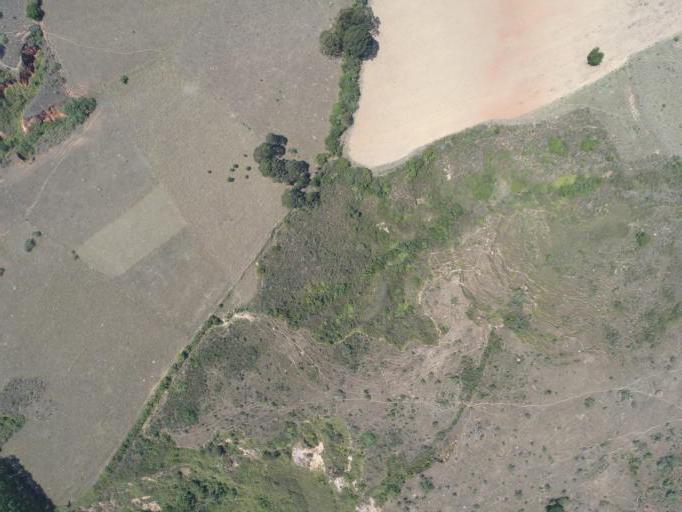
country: BR
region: Minas Gerais
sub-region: Tiradentes
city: Tiradentes
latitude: -21.0430
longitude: -44.1047
